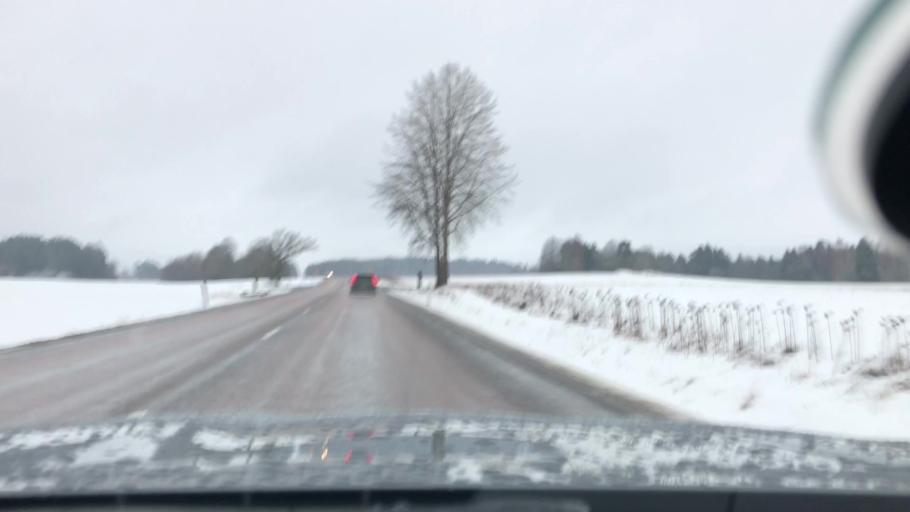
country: SE
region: Stockholm
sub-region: Sodertalje Kommun
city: Pershagen
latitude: 59.0515
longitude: 17.6089
